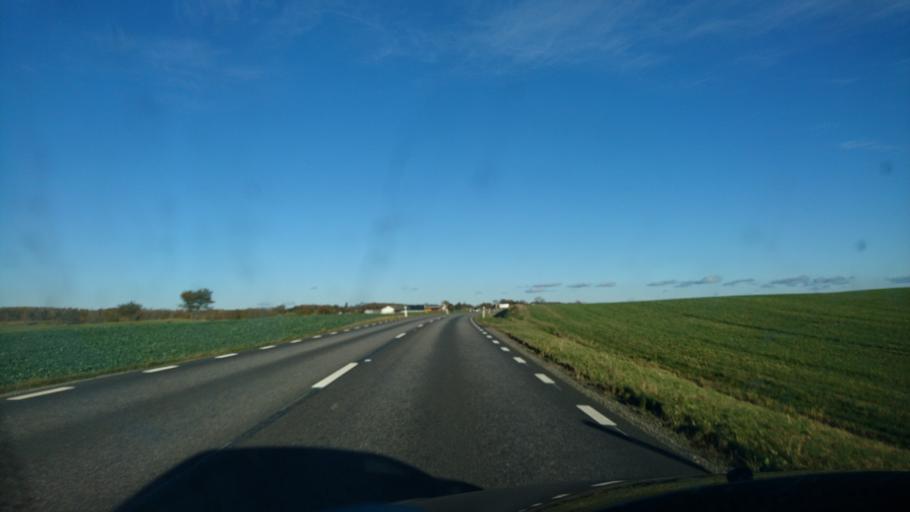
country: SE
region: Skane
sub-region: Tomelilla Kommun
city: Tomelilla
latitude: 55.5909
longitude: 13.9766
